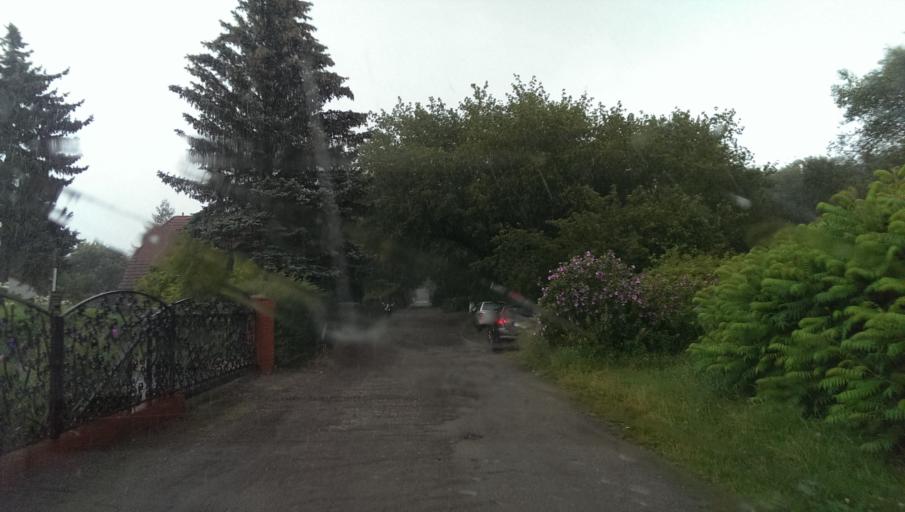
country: DE
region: Brandenburg
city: Teltow
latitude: 52.4016
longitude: 13.2863
